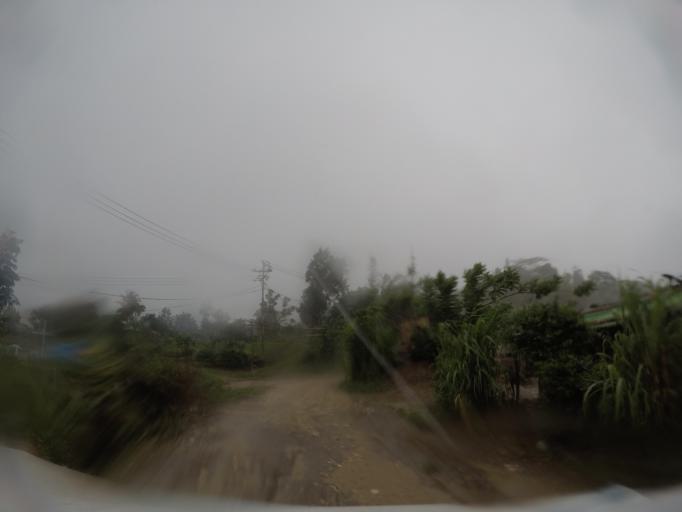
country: TL
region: Baucau
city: Venilale
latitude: -8.6409
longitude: 126.4060
